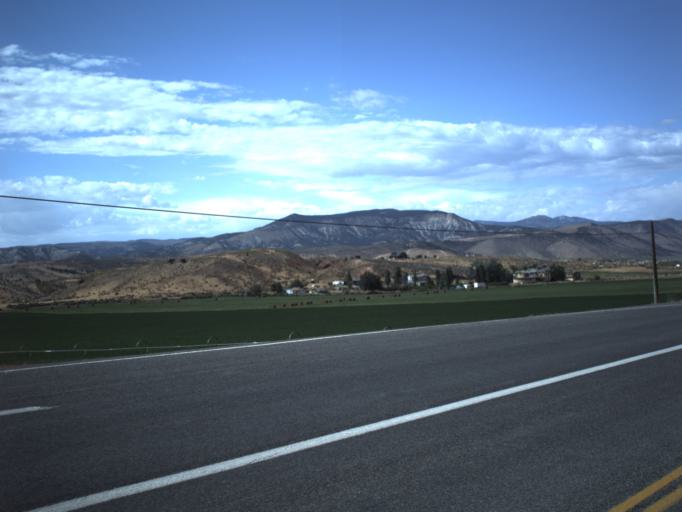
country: US
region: Utah
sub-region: Sanpete County
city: Manti
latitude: 39.1992
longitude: -111.6924
